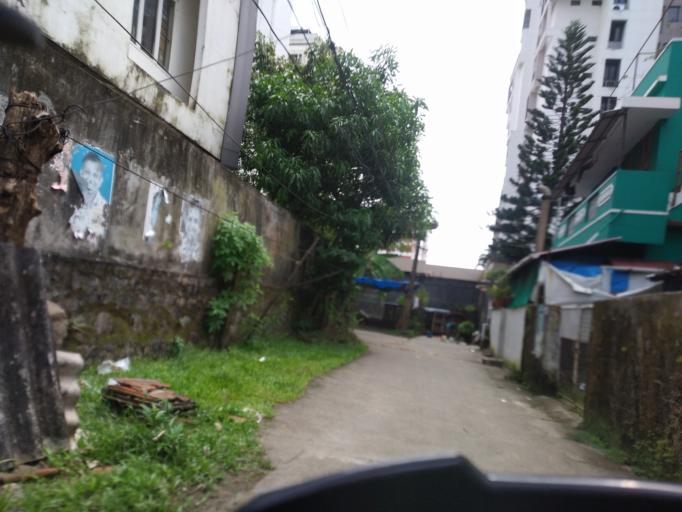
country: IN
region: Kerala
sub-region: Ernakulam
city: Cochin
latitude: 9.9549
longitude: 76.2959
